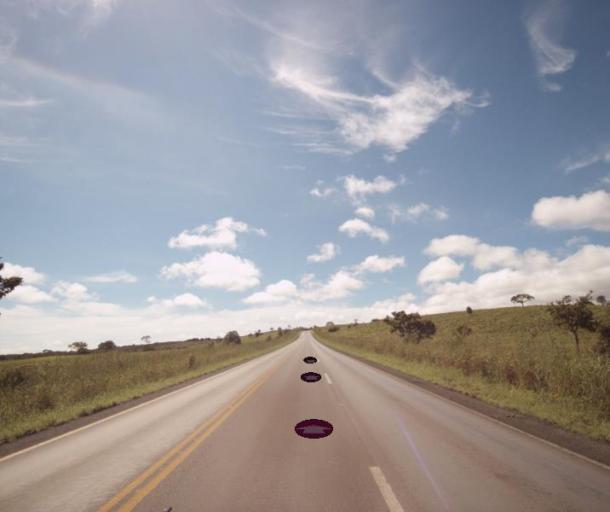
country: BR
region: Goias
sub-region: Padre Bernardo
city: Padre Bernardo
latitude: -15.2201
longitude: -48.5354
